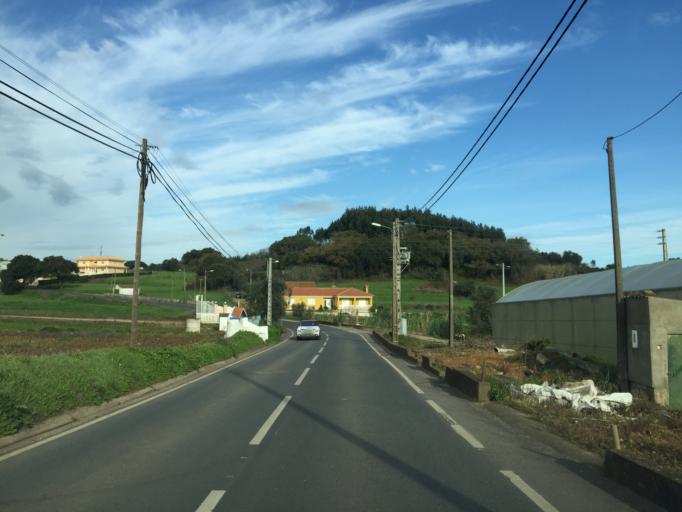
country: PT
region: Lisbon
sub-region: Sintra
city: Almargem
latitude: 38.8425
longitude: -9.2578
